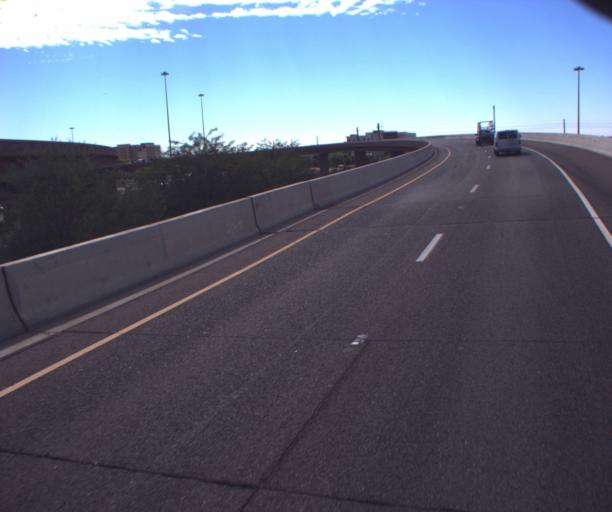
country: US
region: Arizona
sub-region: Maricopa County
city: Chandler
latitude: 33.2941
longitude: -111.8944
